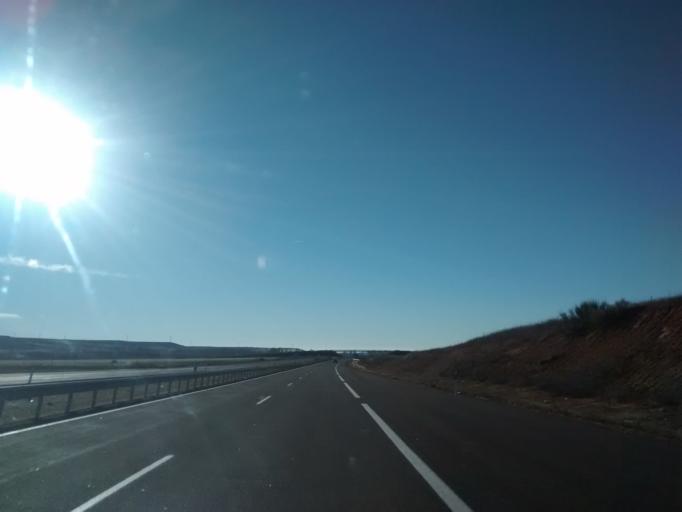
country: ES
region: Castille and Leon
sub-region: Provincia de Palencia
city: Santa Cruz de Boedo
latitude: 42.5095
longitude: -4.3808
